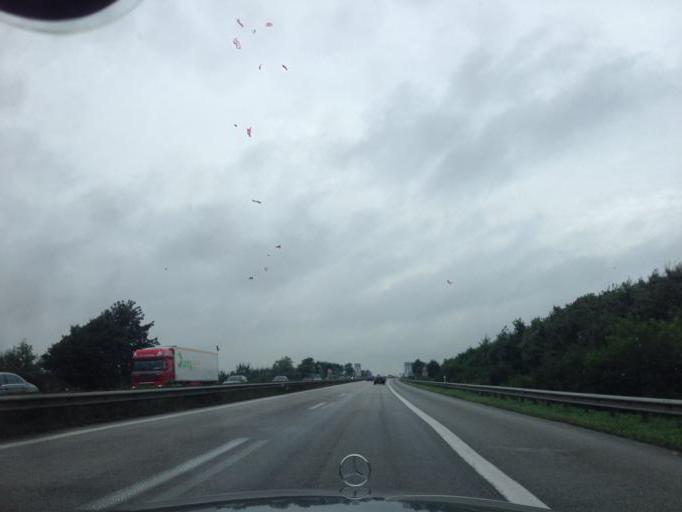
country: DE
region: Schleswig-Holstein
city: Padenstedt
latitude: 54.0720
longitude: 9.9232
